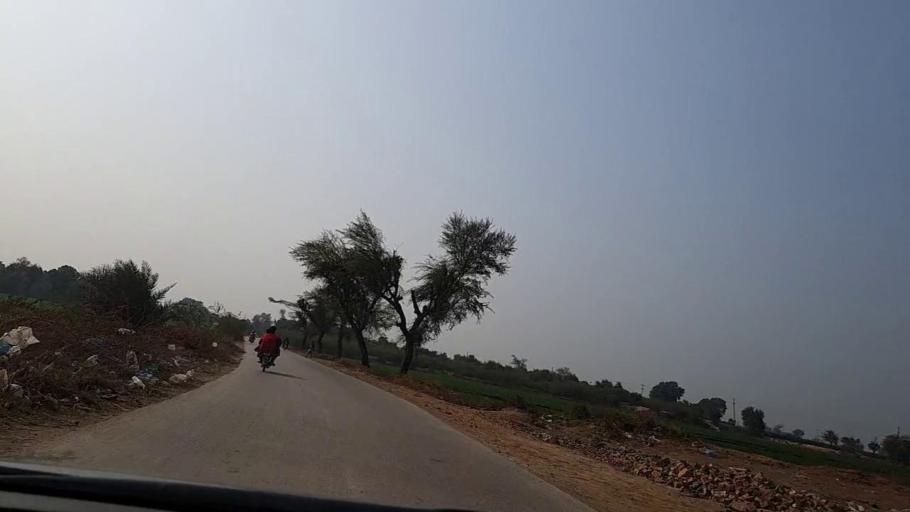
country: PK
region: Sindh
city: Sakrand
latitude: 26.1378
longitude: 68.2511
